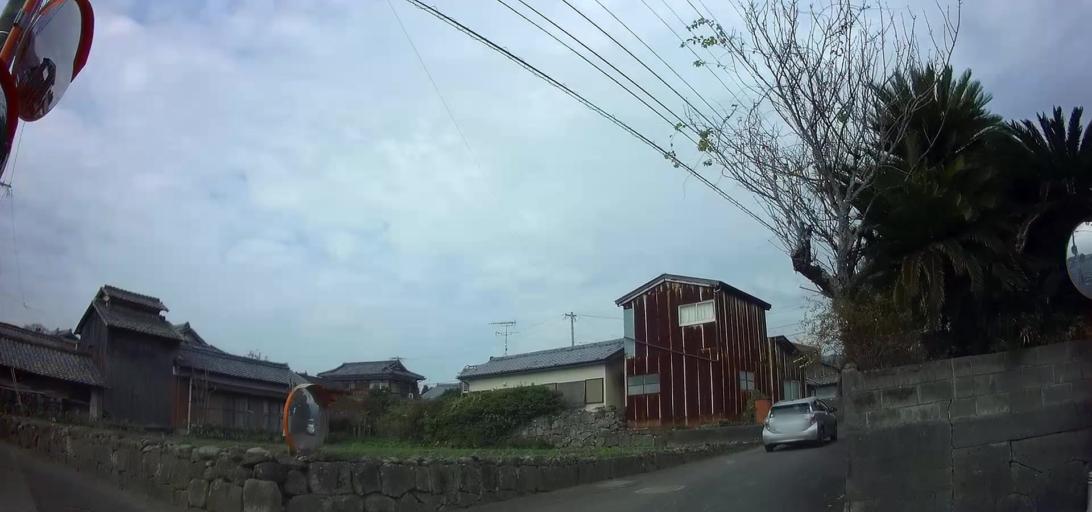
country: JP
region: Nagasaki
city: Shimabara
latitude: 32.6767
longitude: 130.3011
